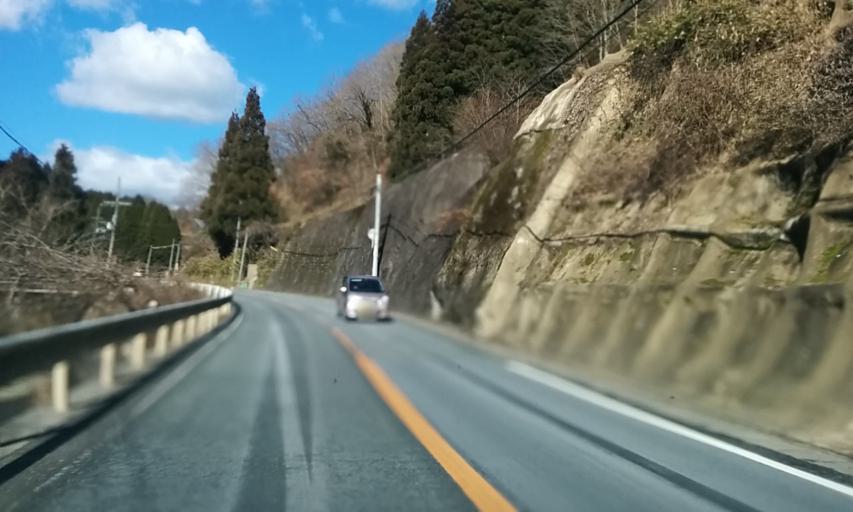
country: JP
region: Kyoto
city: Fukuchiyama
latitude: 35.3439
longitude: 135.0665
